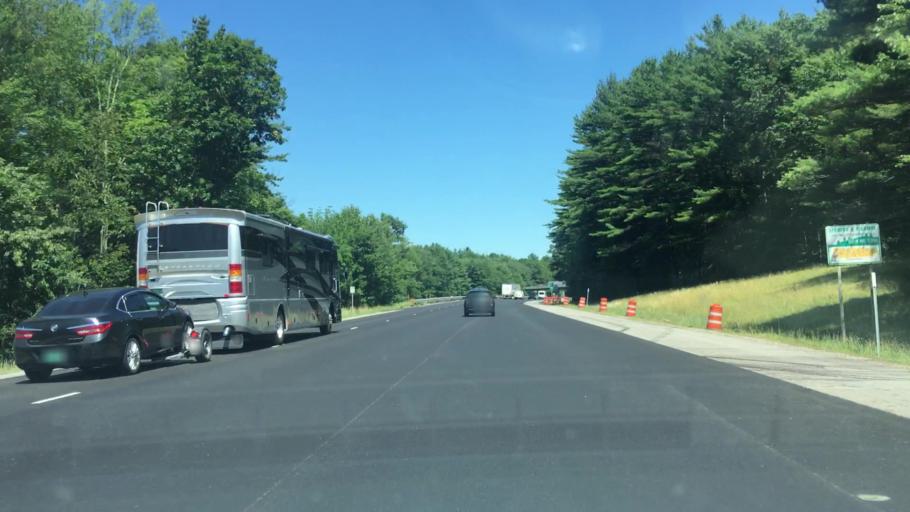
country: US
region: New Hampshire
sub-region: Merrimack County
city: Hopkinton
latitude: 43.1819
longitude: -71.6789
